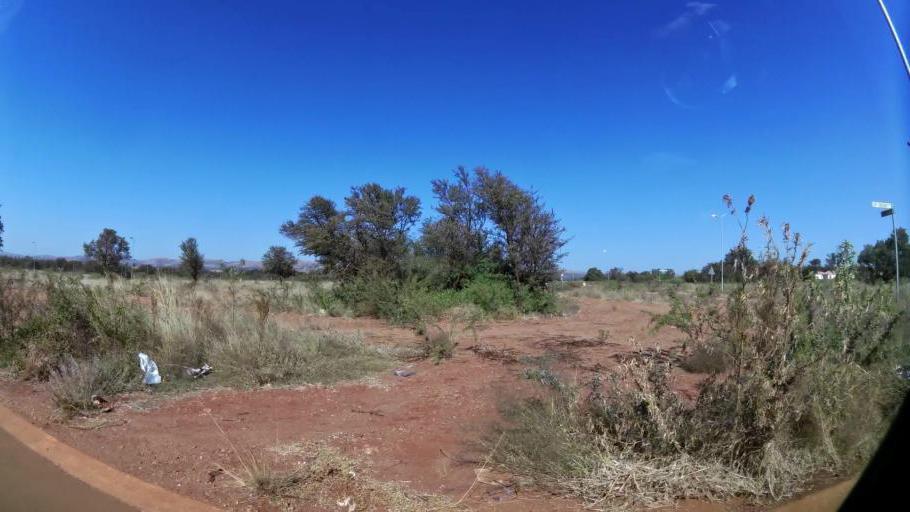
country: ZA
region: North-West
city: Ga-Rankuwa
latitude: -25.6415
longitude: 28.0806
